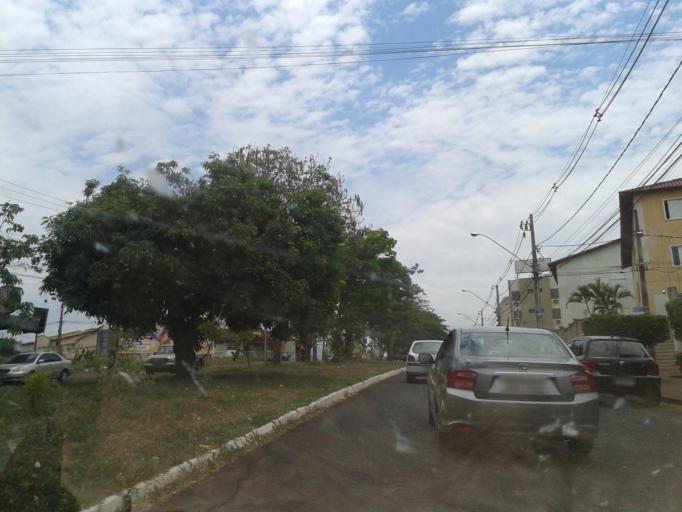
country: BR
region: Minas Gerais
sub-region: Uberlandia
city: Uberlandia
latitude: -18.9146
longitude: -48.3141
